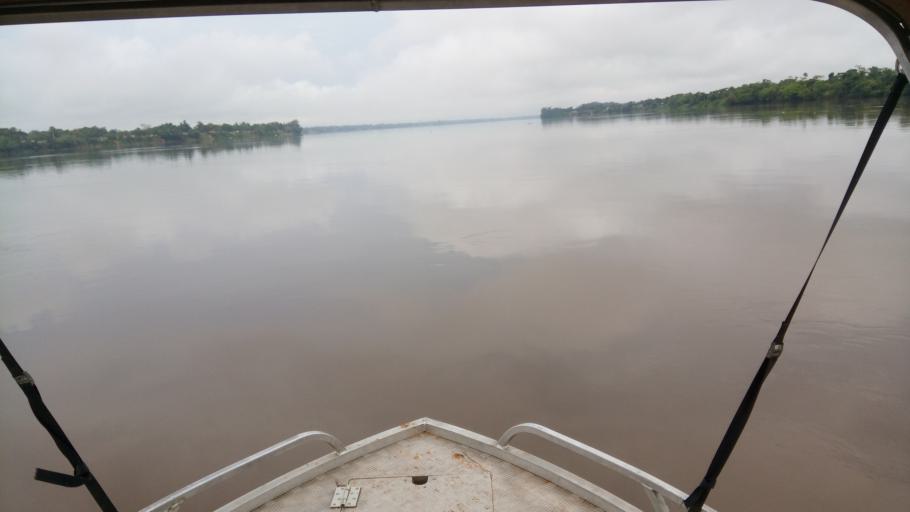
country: CD
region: Eastern Province
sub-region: Sous-Region de la Tshopo
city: Yangambi
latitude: 0.6657
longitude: 24.6199
